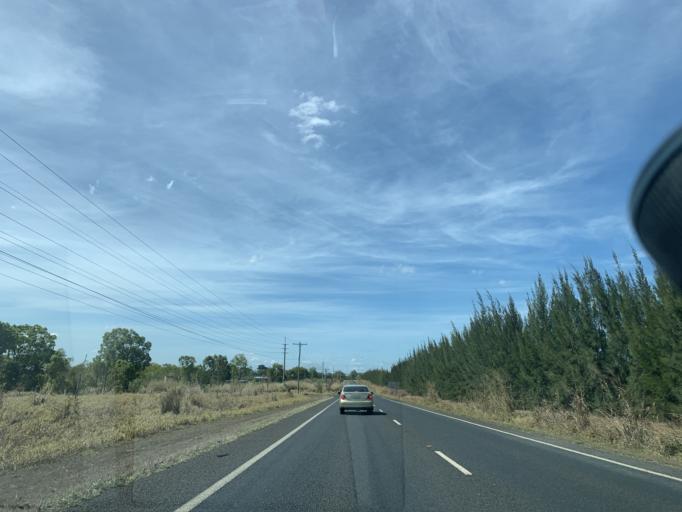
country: AU
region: Queensland
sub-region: Tablelands
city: Mareeba
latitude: -17.0929
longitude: 145.4355
